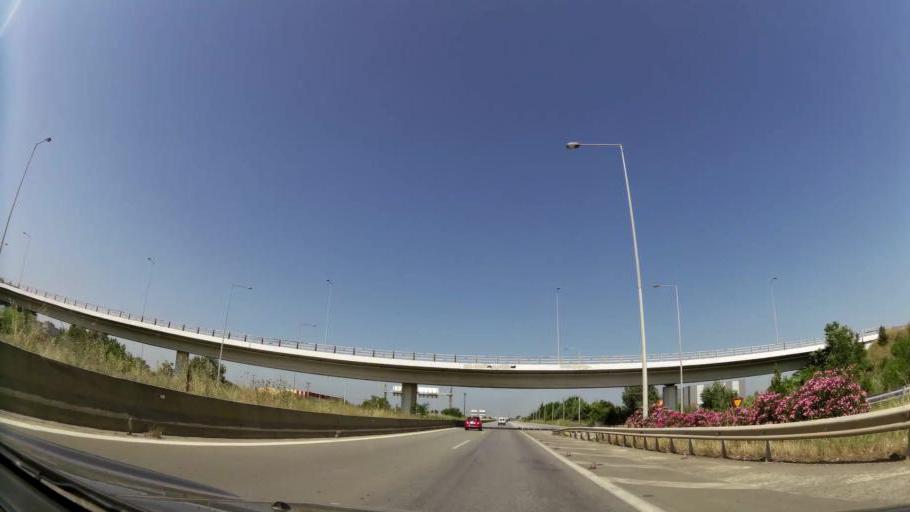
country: GR
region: Central Macedonia
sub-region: Nomos Thessalonikis
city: Kalochori
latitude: 40.6534
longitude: 22.8415
